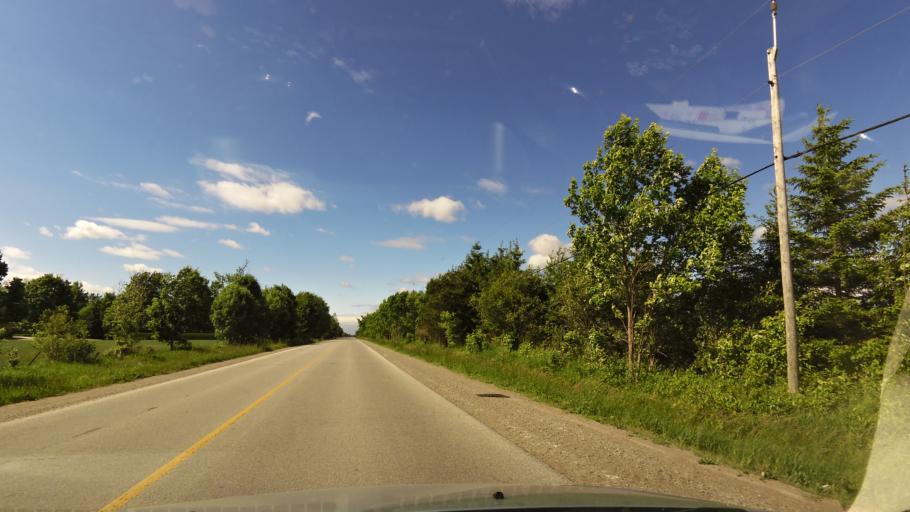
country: CA
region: Ontario
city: Bradford West Gwillimbury
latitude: 44.1452
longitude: -79.6116
